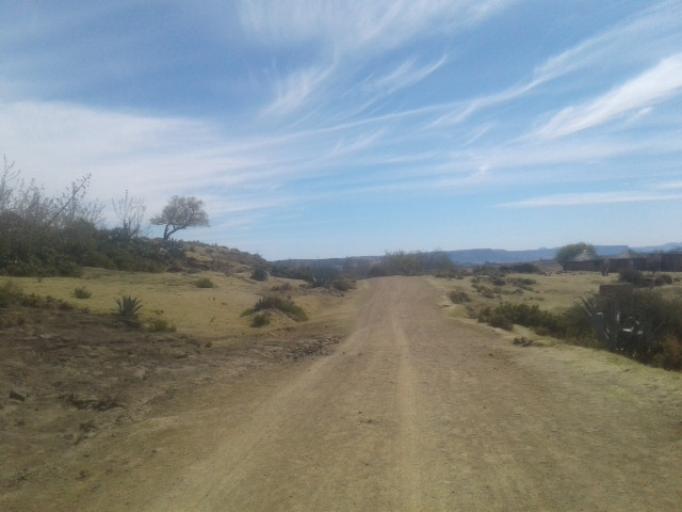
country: LS
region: Maseru
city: Nako
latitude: -29.5439
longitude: 27.6870
